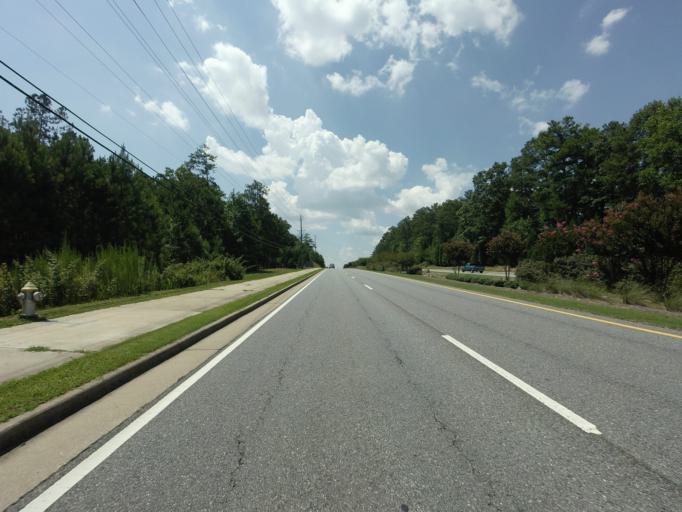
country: US
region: Georgia
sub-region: Fulton County
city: Johns Creek
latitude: 34.0346
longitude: -84.2135
